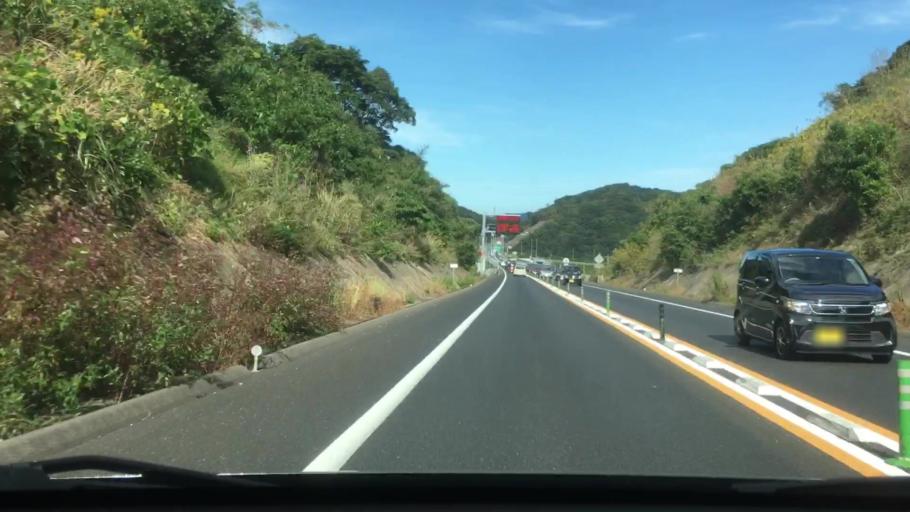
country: JP
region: Nagasaki
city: Sasebo
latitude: 33.1978
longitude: 129.6769
